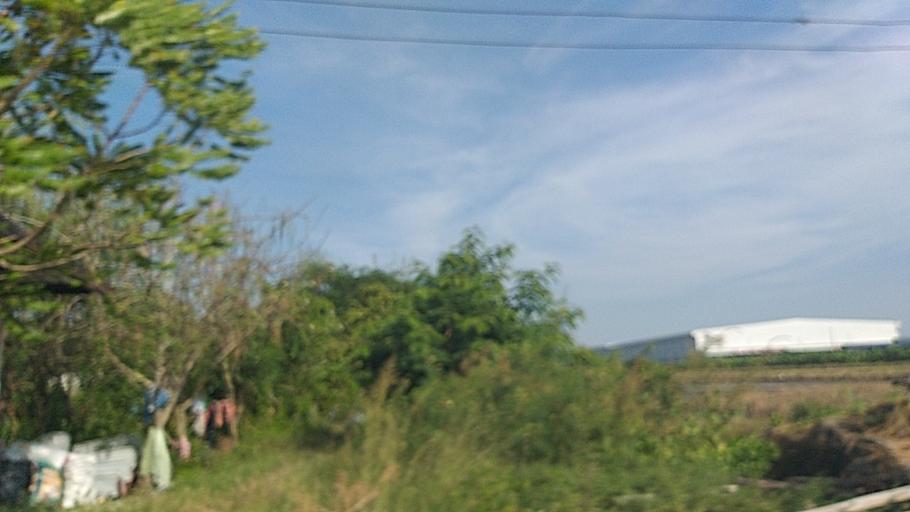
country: TH
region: Pathum Thani
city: Thanyaburi
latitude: 13.9885
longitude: 100.7299
